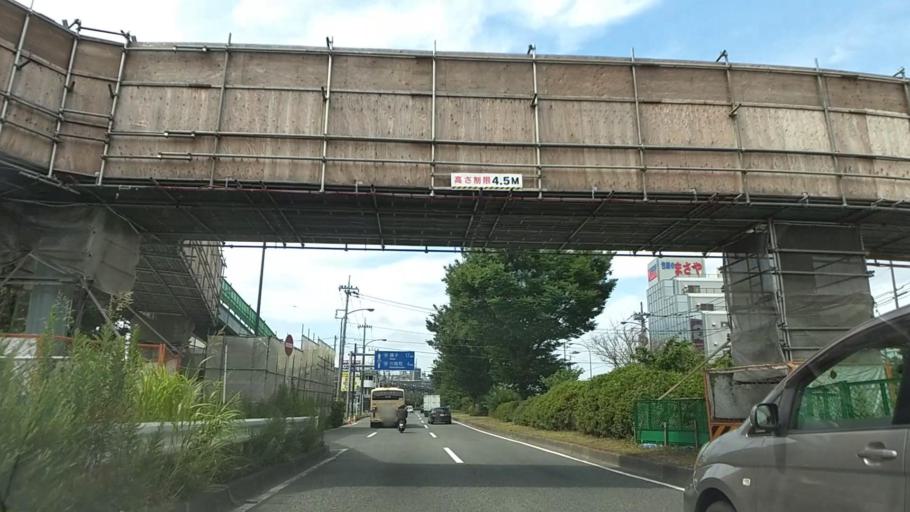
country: JP
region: Kanagawa
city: Yokohama
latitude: 35.5004
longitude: 139.6076
